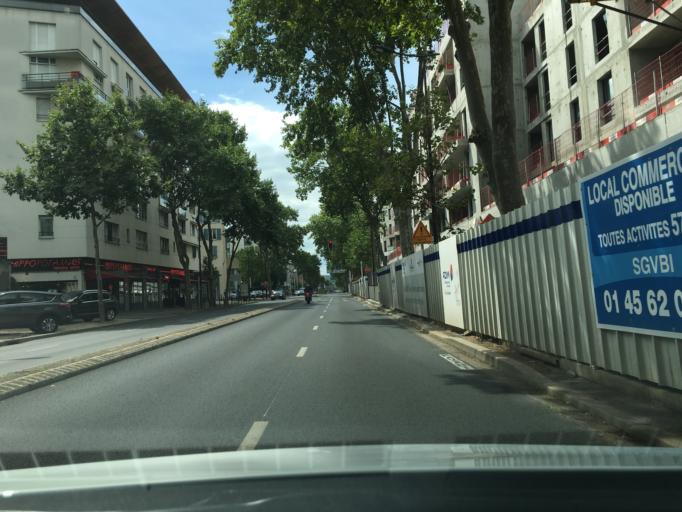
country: FR
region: Ile-de-France
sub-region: Departement des Hauts-de-Seine
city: Rueil-Malmaison
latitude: 48.8835
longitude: 2.1904
